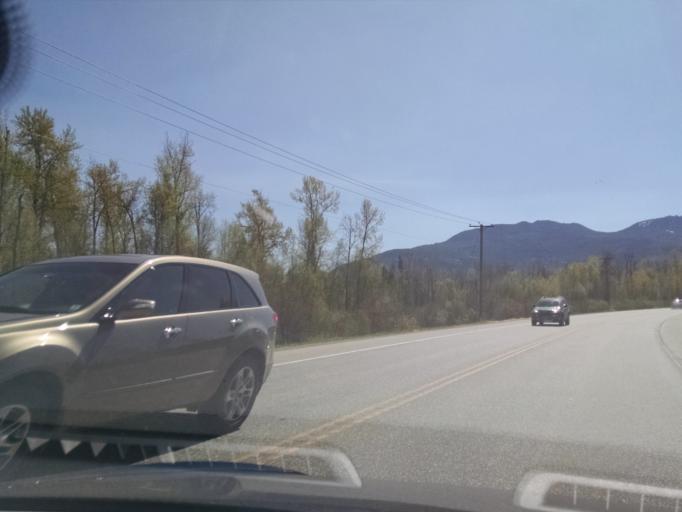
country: CA
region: British Columbia
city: Salmon Arm
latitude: 50.7309
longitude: -119.3158
